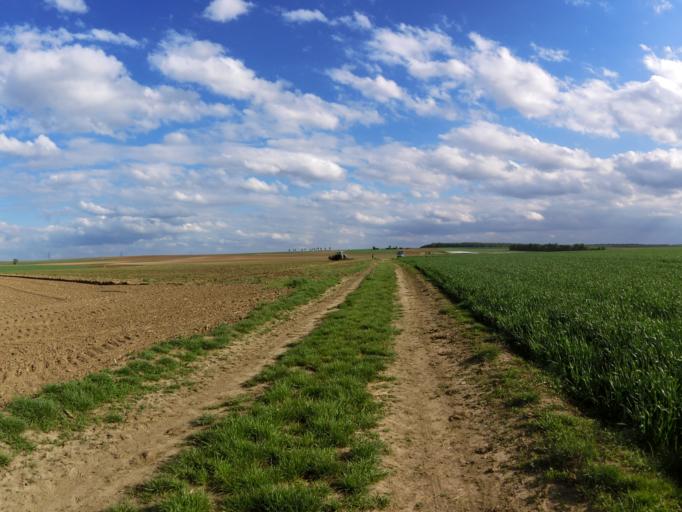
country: DE
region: Bavaria
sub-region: Regierungsbezirk Unterfranken
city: Oberpleichfeld
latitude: 49.8634
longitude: 10.0687
